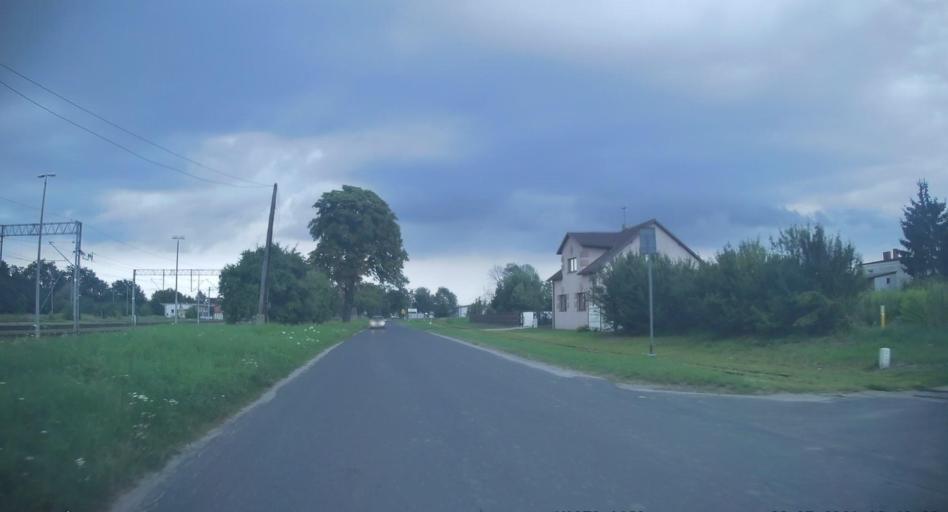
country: PL
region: Lodz Voivodeship
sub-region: Powiat brzezinski
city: Rogow
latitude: 51.8154
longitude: 19.8831
